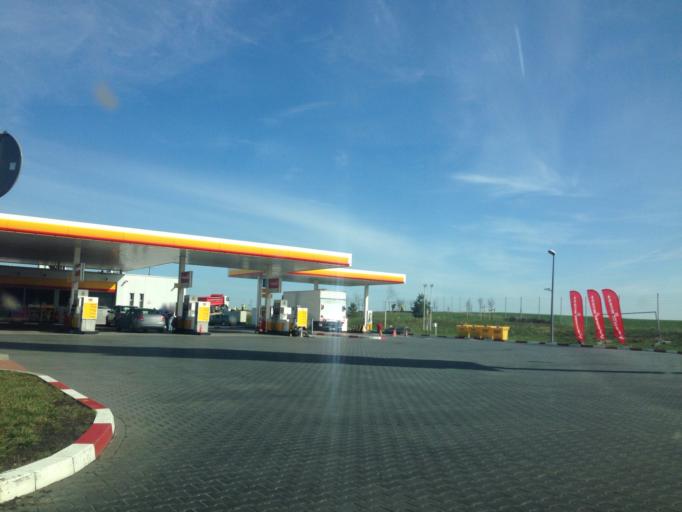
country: PL
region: Pomeranian Voivodeship
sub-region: Powiat starogardzki
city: Bobowo
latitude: 53.8870
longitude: 18.6308
